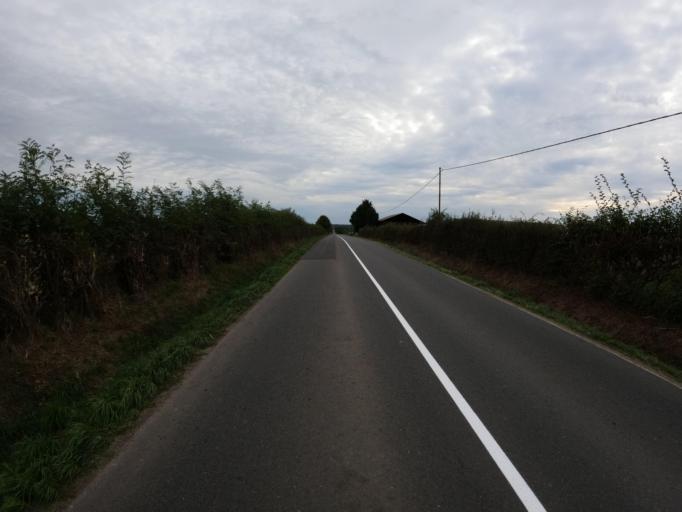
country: FR
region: Poitou-Charentes
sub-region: Departement de la Vienne
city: Saulge
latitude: 46.3842
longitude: 0.8486
